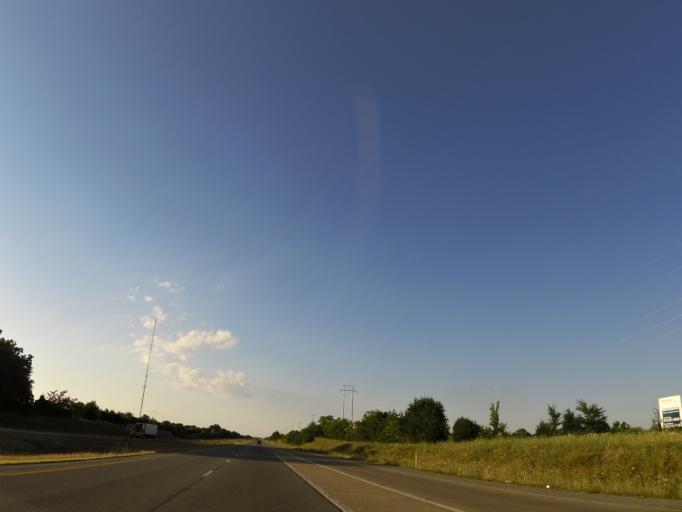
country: US
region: Tennessee
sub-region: Wilson County
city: Rural Hill
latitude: 36.0729
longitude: -86.4295
